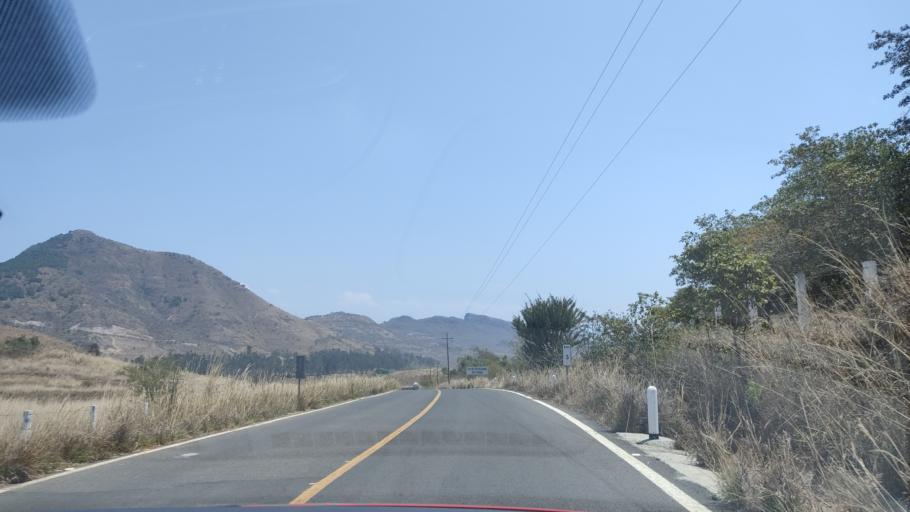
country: MX
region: Nayarit
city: Puga
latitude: 21.6101
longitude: -104.7300
